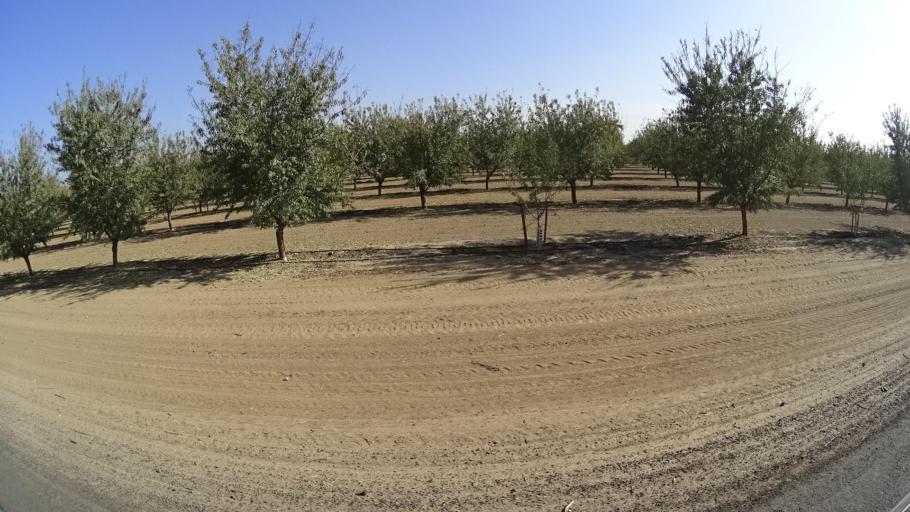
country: US
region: California
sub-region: Kern County
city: McFarland
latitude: 35.6541
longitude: -119.1868
